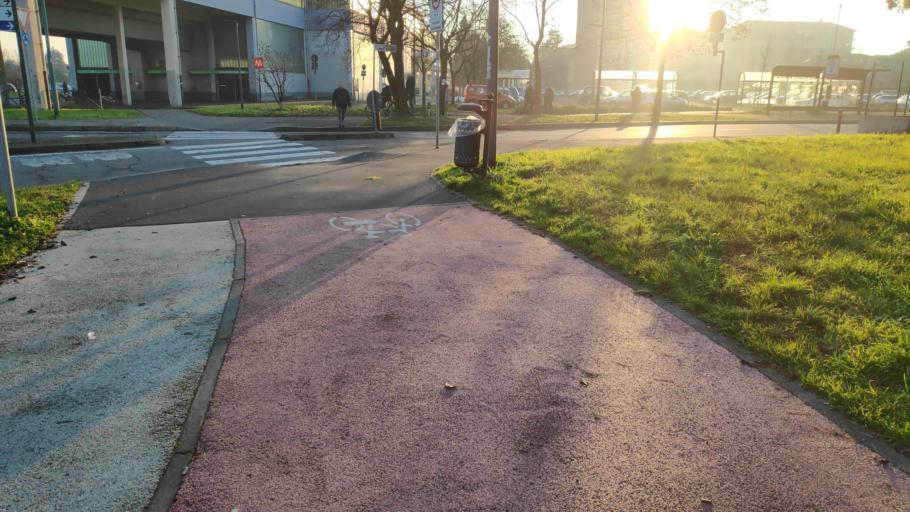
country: IT
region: Lombardy
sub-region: Citta metropolitana di Milano
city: Cologno Monzese
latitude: 45.5284
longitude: 9.2831
